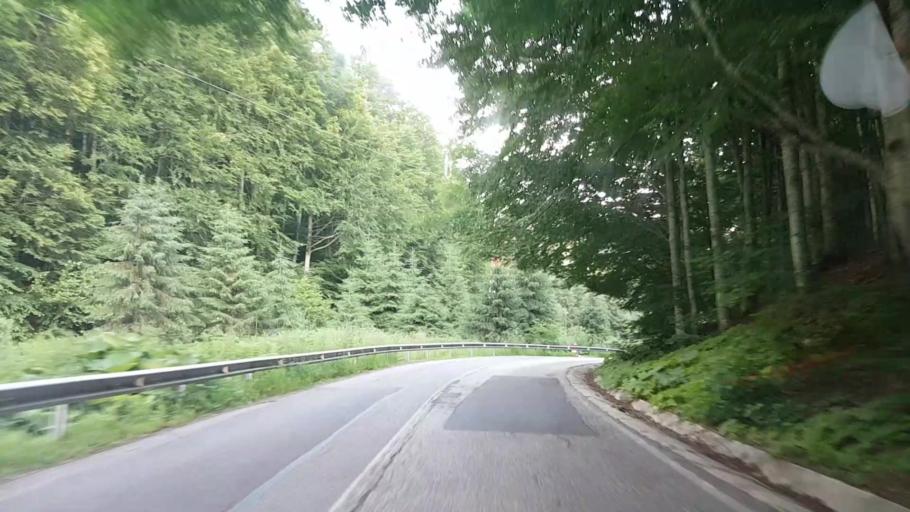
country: RO
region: Harghita
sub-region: Comuna Praid
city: Ocna de Sus
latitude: 46.5956
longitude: 25.2411
